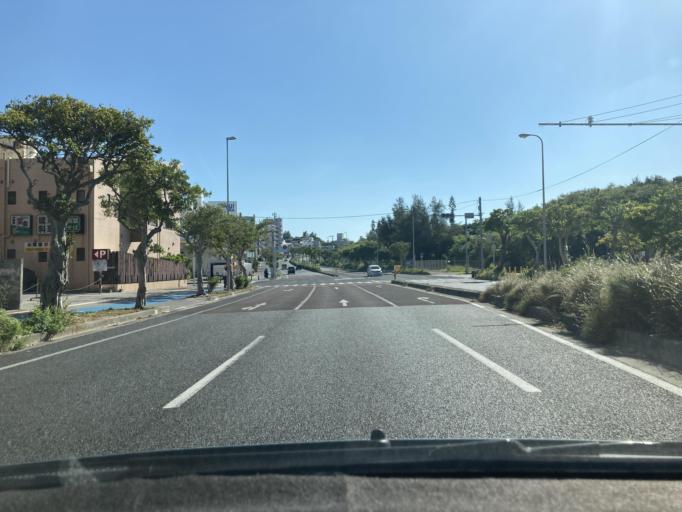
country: JP
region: Okinawa
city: Naha-shi
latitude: 26.2028
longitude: 127.6622
